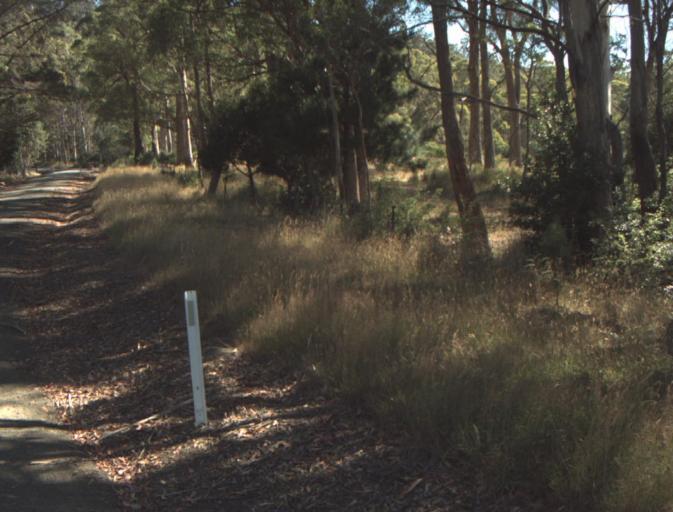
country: AU
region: Tasmania
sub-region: Launceston
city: Newstead
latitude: -41.3283
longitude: 147.3418
